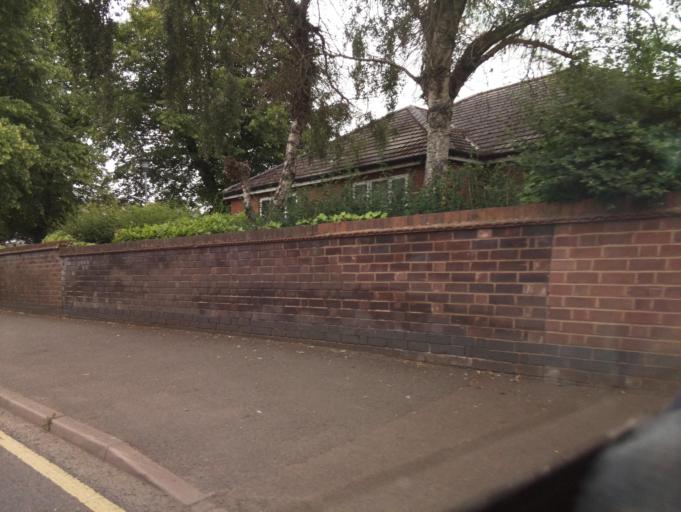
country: GB
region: England
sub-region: Staffordshire
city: Burton upon Trent
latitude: 52.8155
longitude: -1.6380
